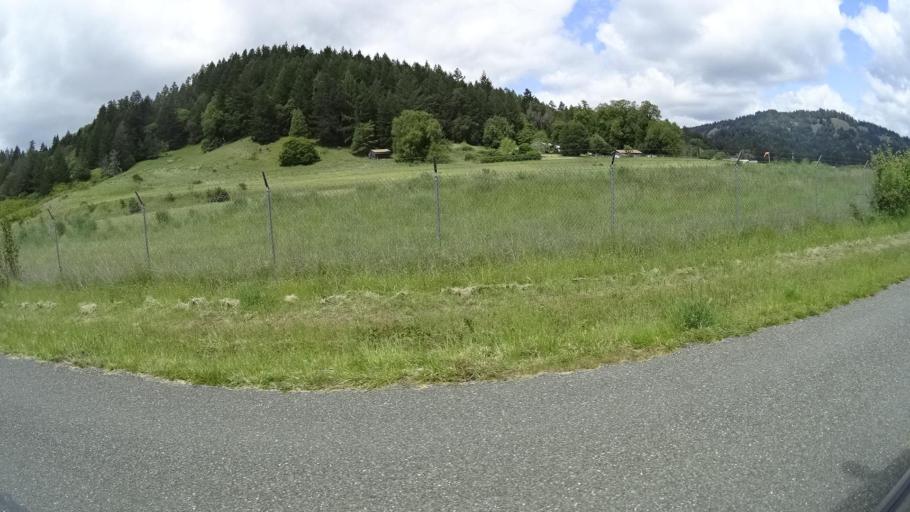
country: US
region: California
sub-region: Humboldt County
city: Redway
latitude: 40.0826
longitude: -123.8144
